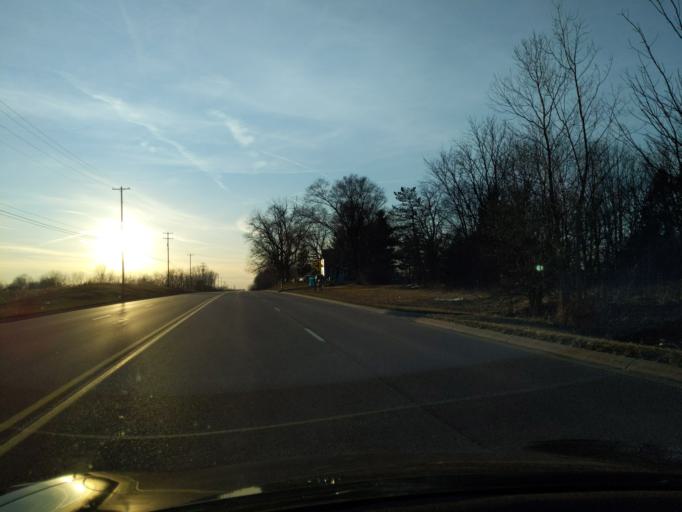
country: US
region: Michigan
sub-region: Ingham County
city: Holt
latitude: 42.6403
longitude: -84.4893
